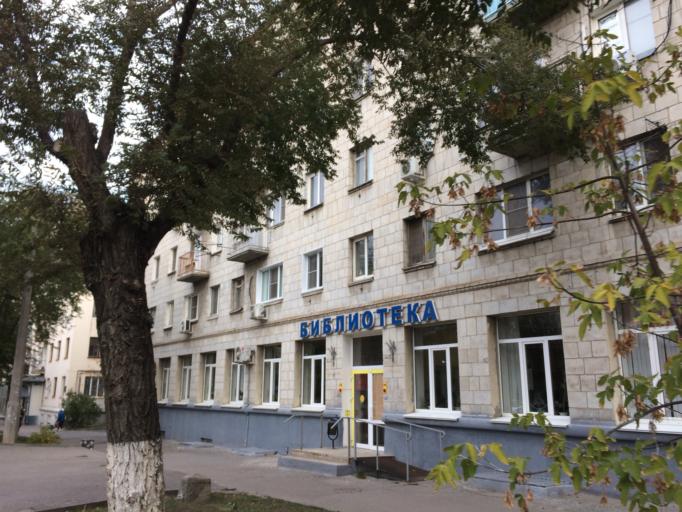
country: RU
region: Volgograd
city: Volgograd
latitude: 48.7194
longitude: 44.5322
